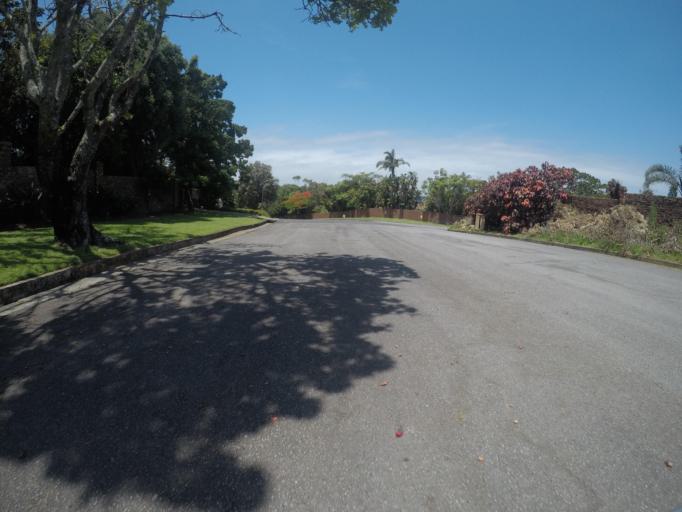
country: ZA
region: Eastern Cape
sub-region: Buffalo City Metropolitan Municipality
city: East London
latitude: -32.9992
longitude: 27.9256
